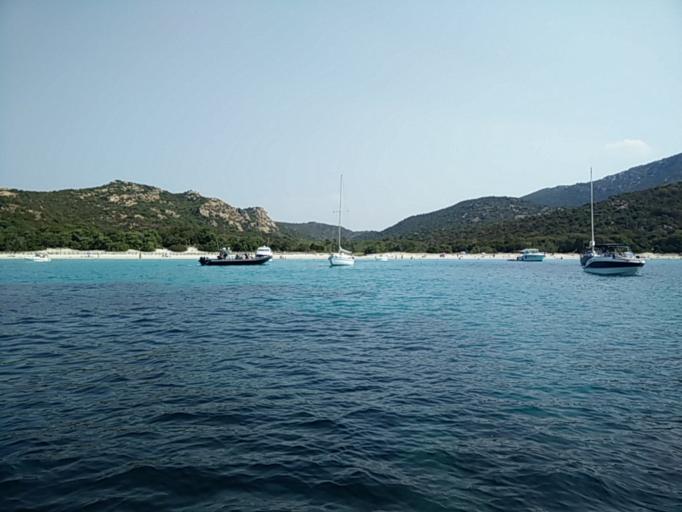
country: FR
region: Corsica
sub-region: Departement de la Corse-du-Sud
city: Sartene
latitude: 41.4942
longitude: 8.9339
